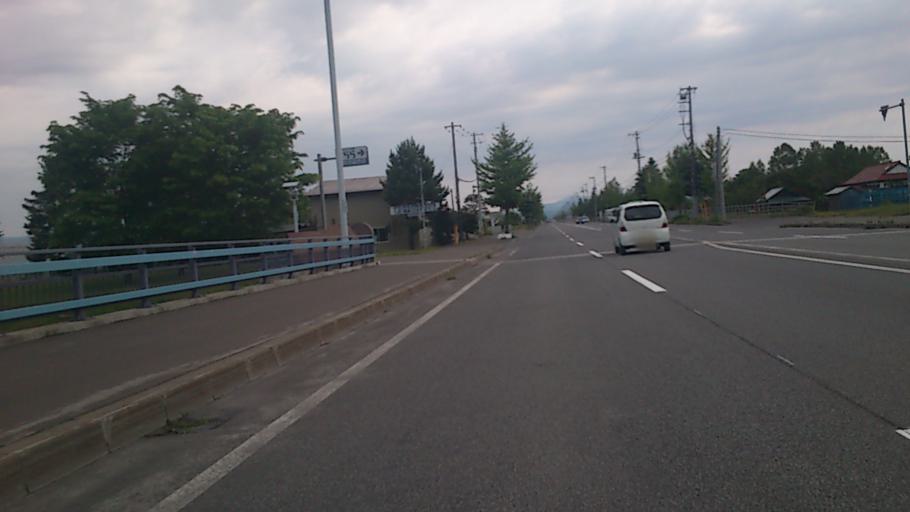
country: JP
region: Hokkaido
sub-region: Asahikawa-shi
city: Asahikawa
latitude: 43.8217
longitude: 142.4517
